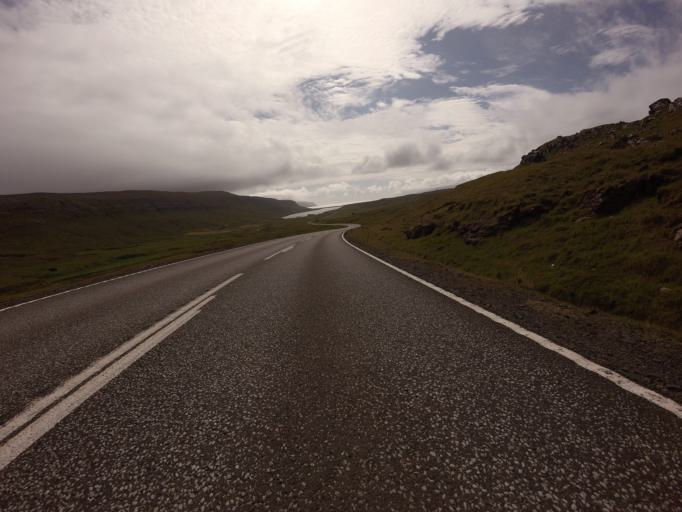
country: FO
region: Sandoy
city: Sandur
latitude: 61.8692
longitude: -6.8450
